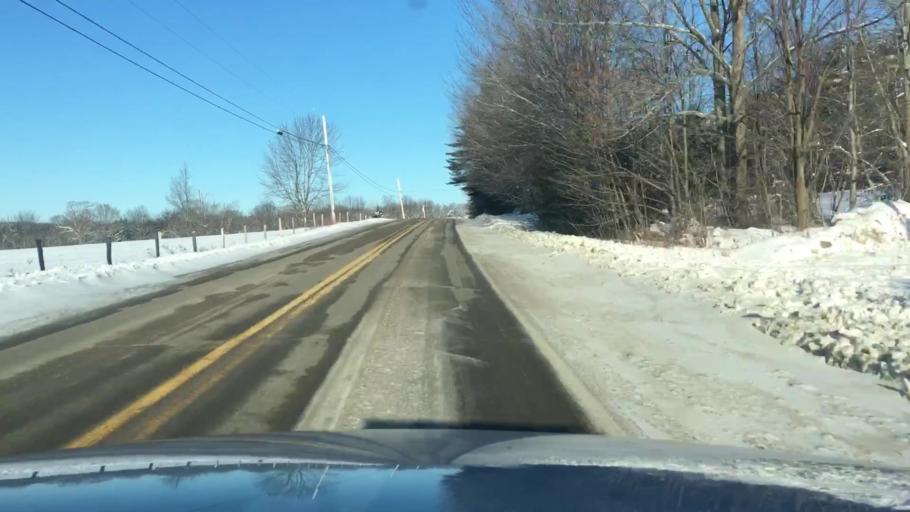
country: US
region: Maine
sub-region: Kennebec County
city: Readfield
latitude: 44.4258
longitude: -69.9334
